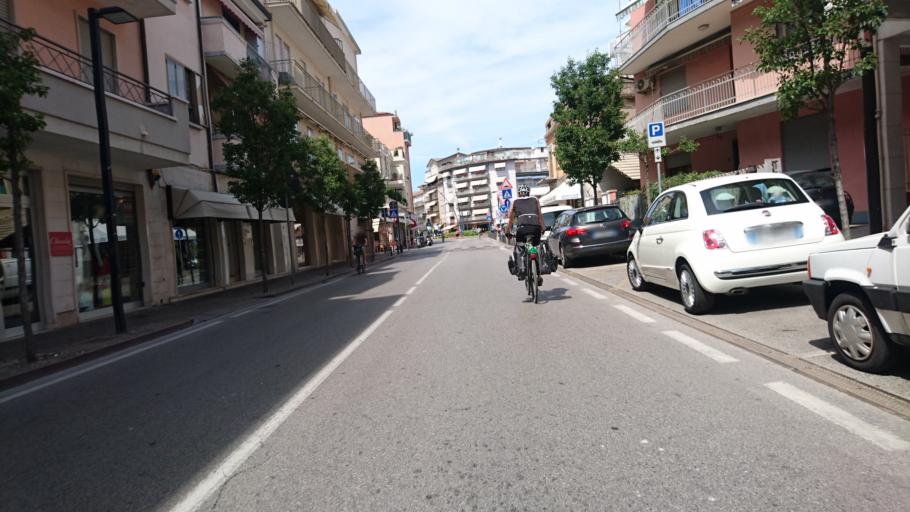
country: IT
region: Veneto
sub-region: Provincia di Venezia
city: Chioggia
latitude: 45.2139
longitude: 12.2926
